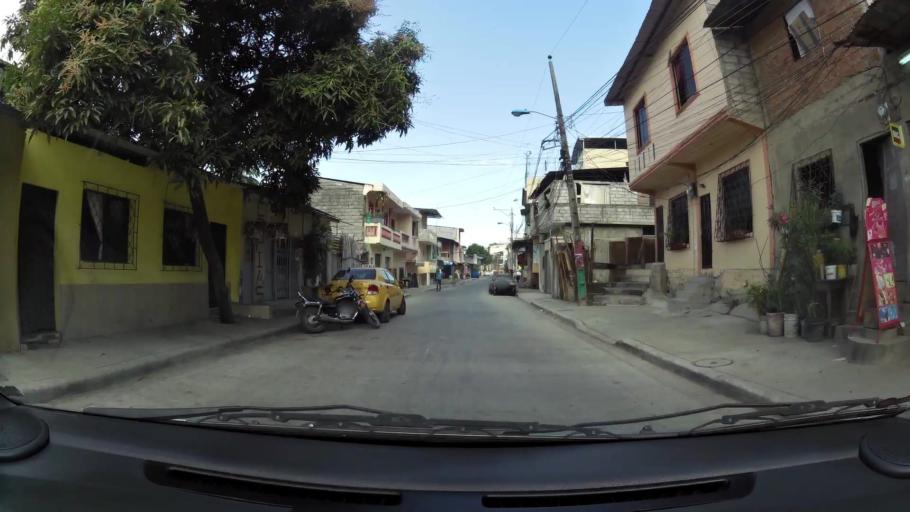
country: EC
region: Guayas
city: Guayaquil
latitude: -2.1502
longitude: -79.9365
